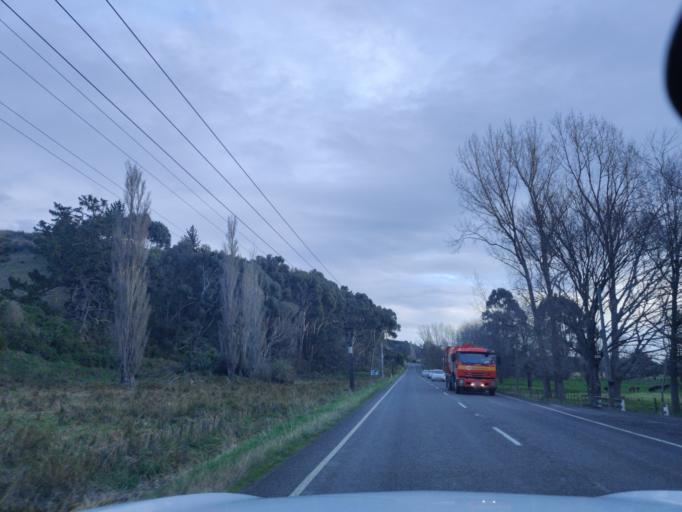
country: NZ
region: Manawatu-Wanganui
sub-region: Palmerston North City
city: Palmerston North
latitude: -40.3701
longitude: 175.6563
